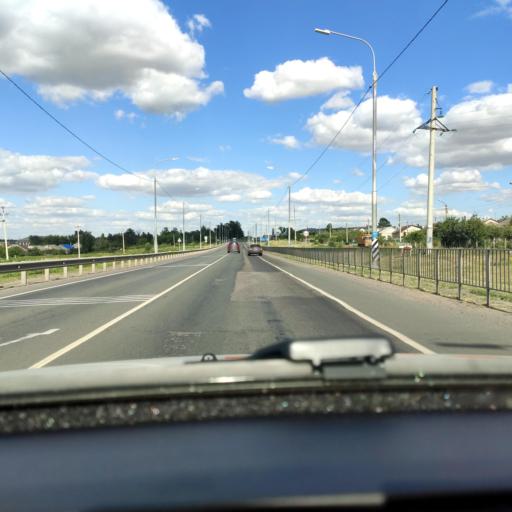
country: RU
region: Voronezj
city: Kashirskoye
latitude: 51.4976
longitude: 39.5566
